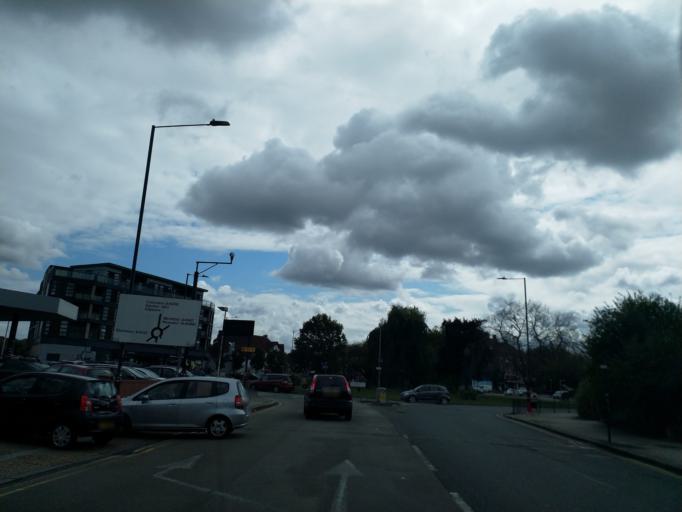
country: GB
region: England
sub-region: Greater London
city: Edgware
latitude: 51.5851
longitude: -0.2829
